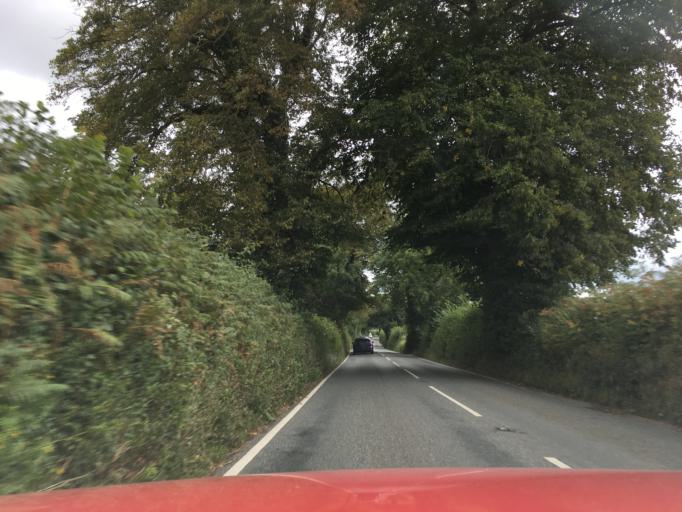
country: GB
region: England
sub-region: Devon
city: Exminster
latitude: 50.6485
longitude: -3.4810
